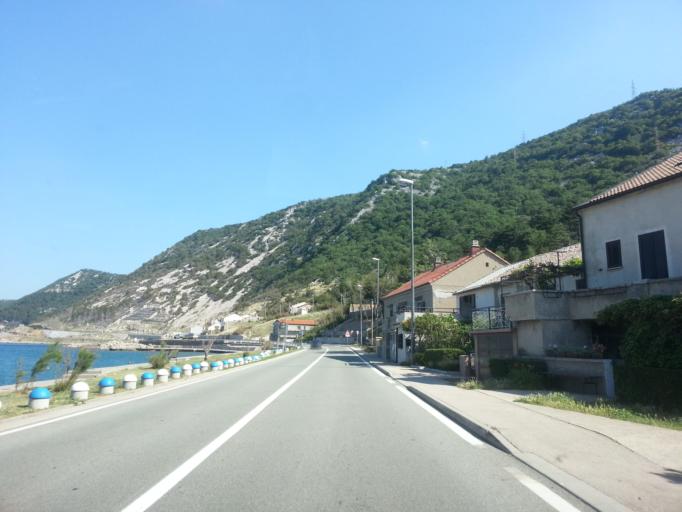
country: HR
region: Primorsko-Goranska
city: Kraljevica
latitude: 45.2807
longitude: 14.5816
